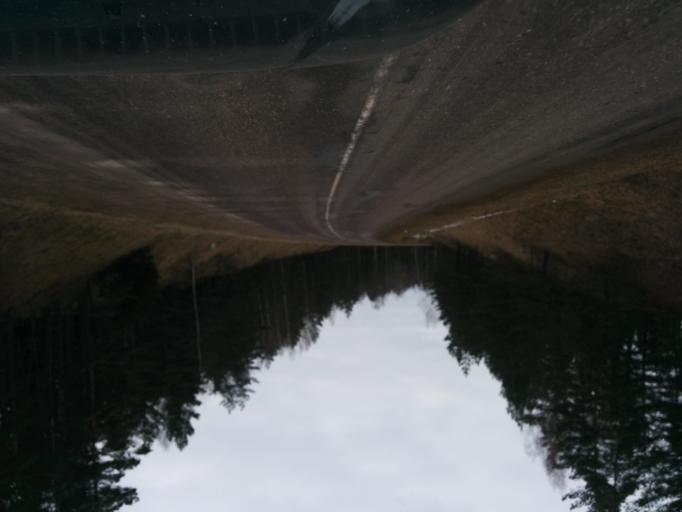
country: LV
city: Tireli
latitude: 56.8878
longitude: 23.5382
